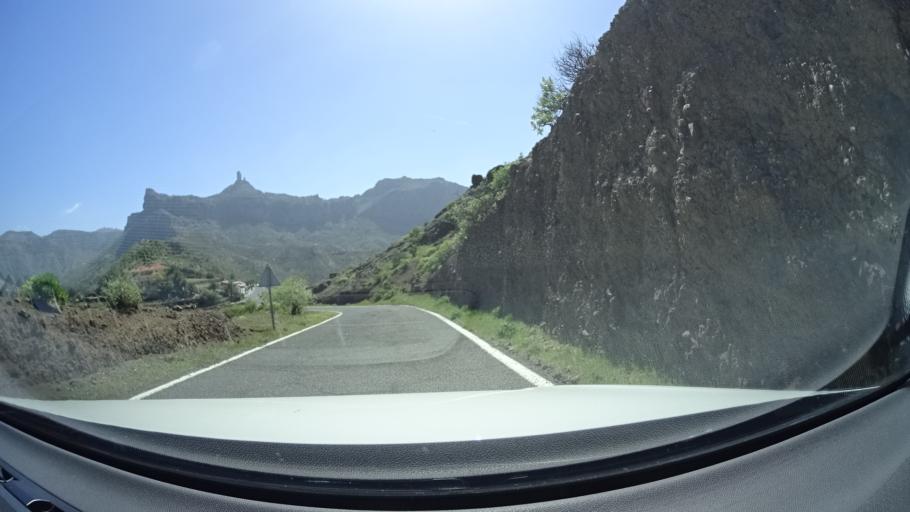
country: ES
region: Canary Islands
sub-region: Provincia de Las Palmas
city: Tejeda
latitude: 27.9891
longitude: -15.6325
